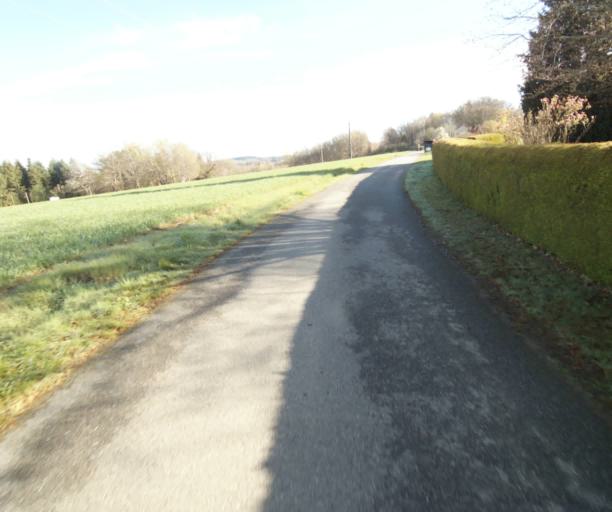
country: FR
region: Limousin
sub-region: Departement de la Correze
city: Laguenne
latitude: 45.2855
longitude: 1.8481
